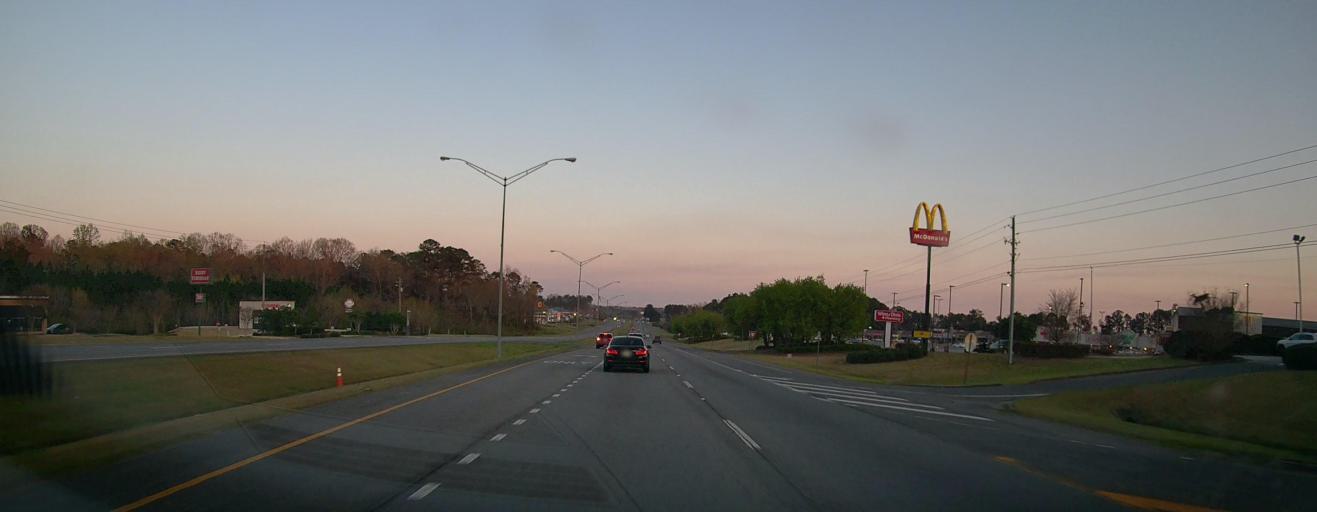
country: US
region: Alabama
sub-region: Tallapoosa County
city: Alexander City
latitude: 32.9237
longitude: -85.9607
